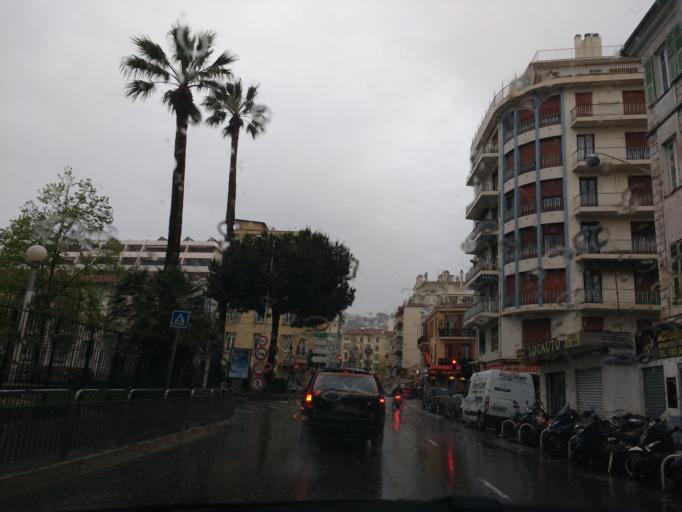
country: FR
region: Provence-Alpes-Cote d'Azur
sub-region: Departement des Alpes-Maritimes
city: Nice
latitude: 43.7061
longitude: 7.2584
